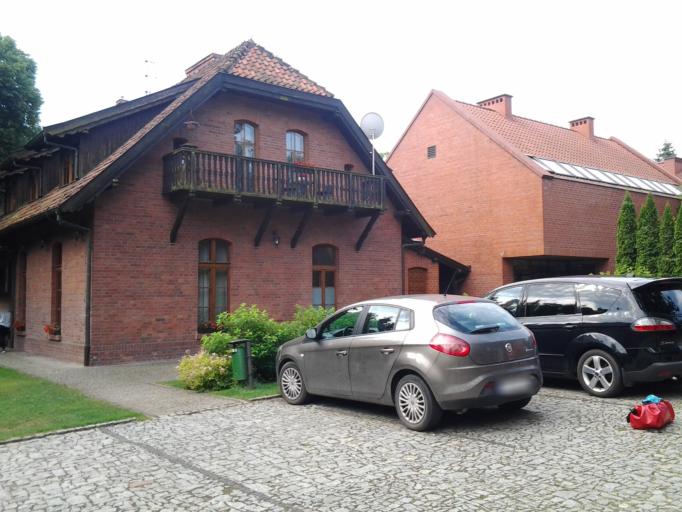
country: PL
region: Greater Poland Voivodeship
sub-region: Powiat sredzki
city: Zaniemysl
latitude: 52.1444
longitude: 17.1597
